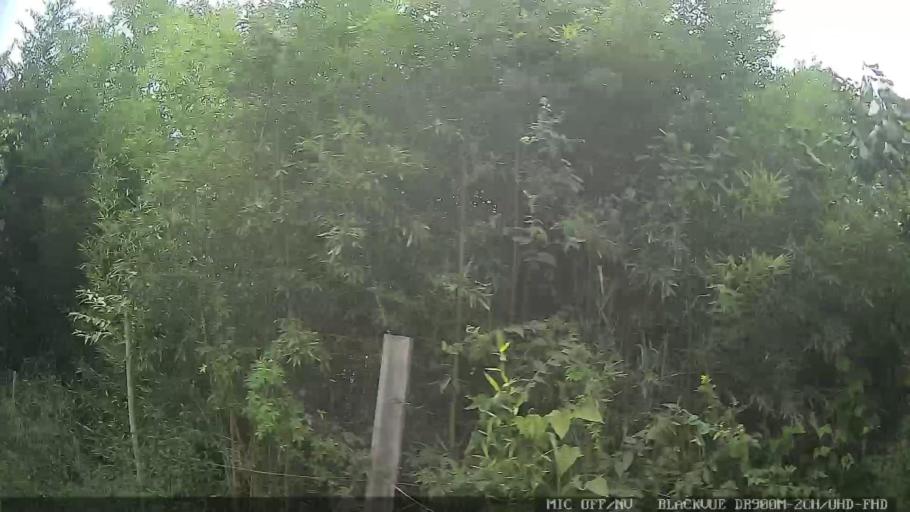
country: BR
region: Sao Paulo
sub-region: Santa Isabel
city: Santa Isabel
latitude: -23.3869
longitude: -46.2355
